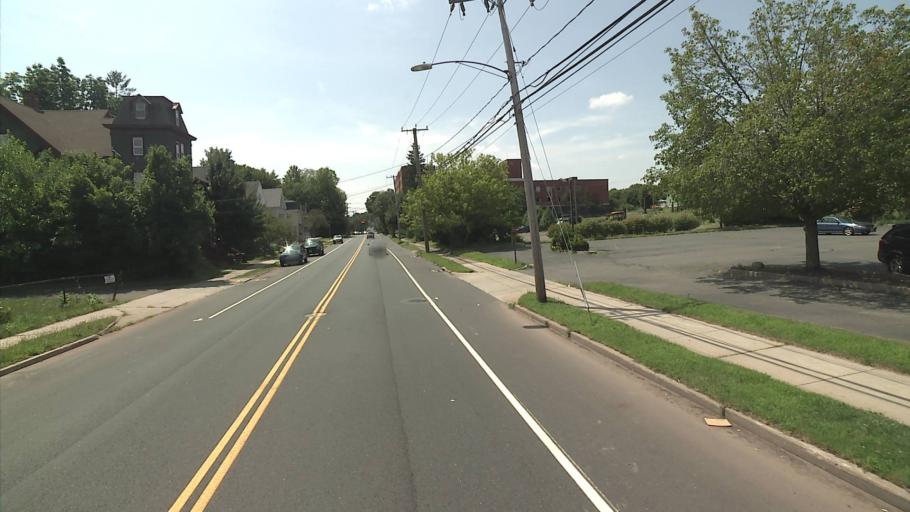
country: US
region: Connecticut
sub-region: New Haven County
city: Meriden
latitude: 41.5350
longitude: -72.8080
